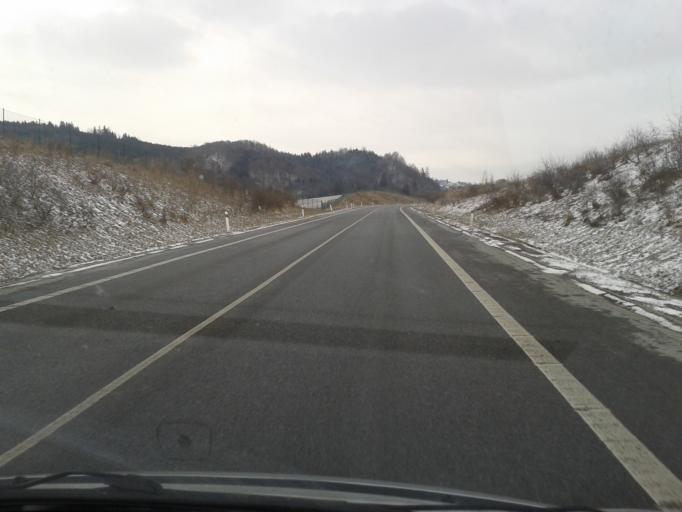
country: SK
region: Zilinsky
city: Tvrdosin
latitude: 49.3479
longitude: 19.5826
